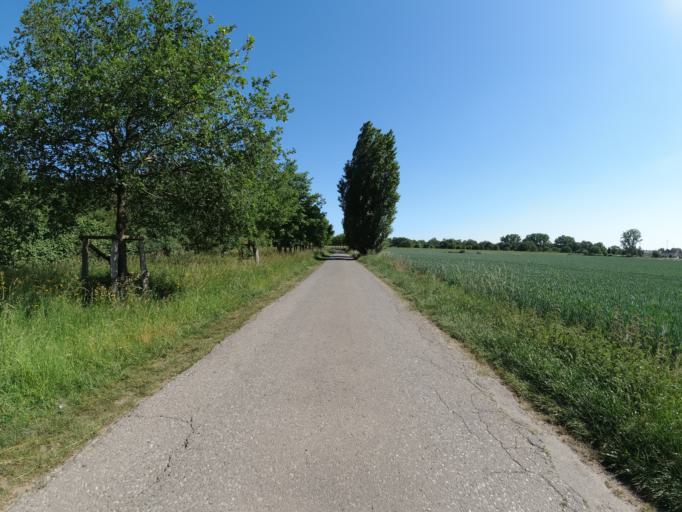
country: DE
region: North Rhine-Westphalia
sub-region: Regierungsbezirk Dusseldorf
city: Hochfeld
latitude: 51.3823
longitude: 6.6936
